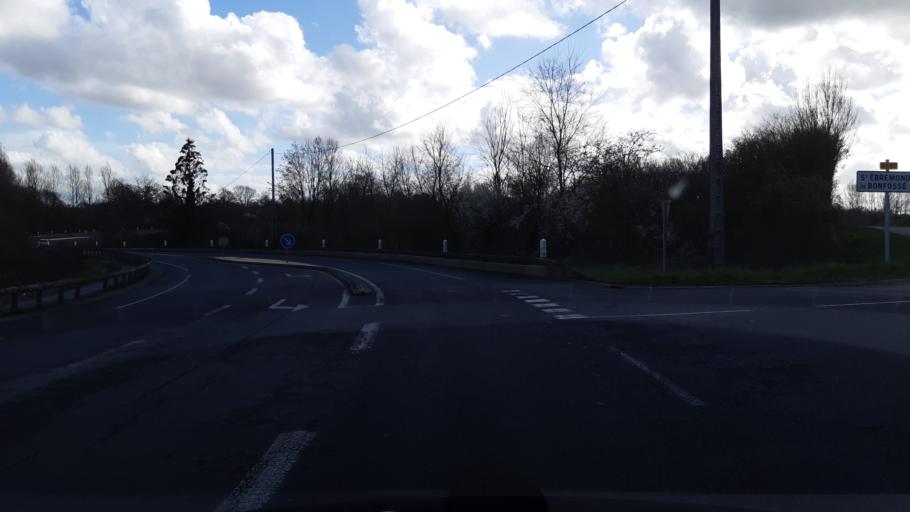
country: FR
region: Lower Normandy
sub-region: Departement de la Manche
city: Agneaux
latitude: 49.0711
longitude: -1.1305
